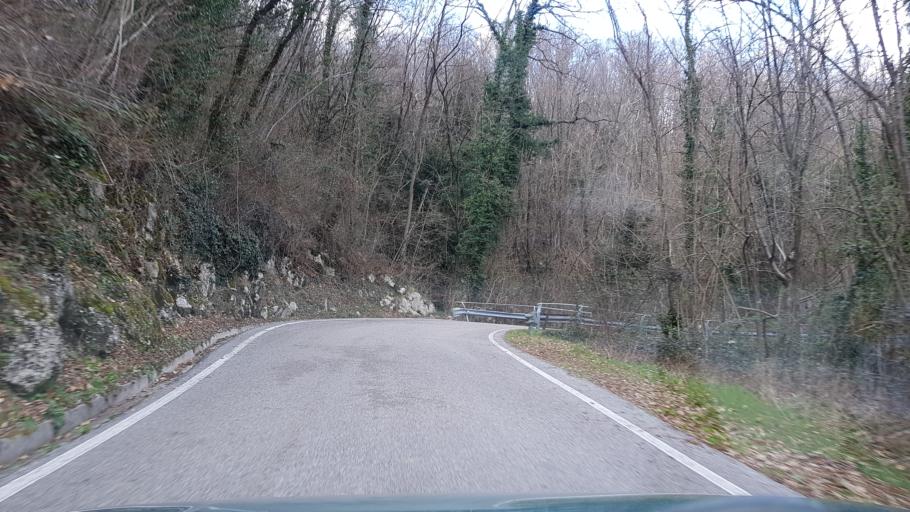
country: IT
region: Friuli Venezia Giulia
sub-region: Provincia di Udine
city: Faedis
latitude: 46.1680
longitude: 13.3586
